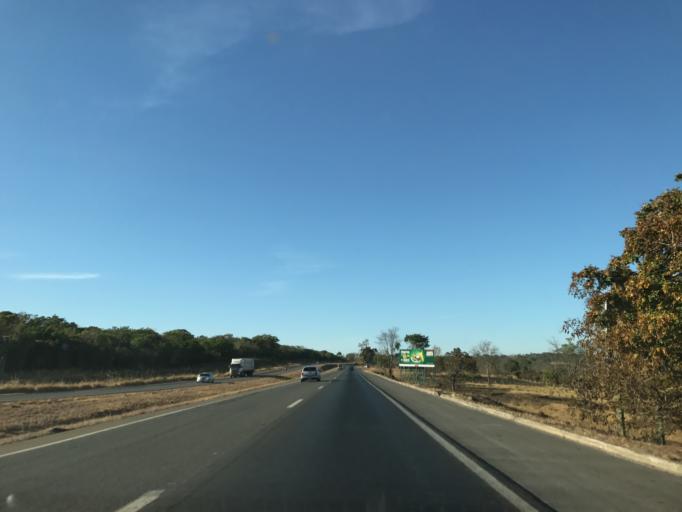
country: BR
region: Goias
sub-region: Hidrolandia
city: Hidrolandia
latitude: -16.9061
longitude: -49.2541
